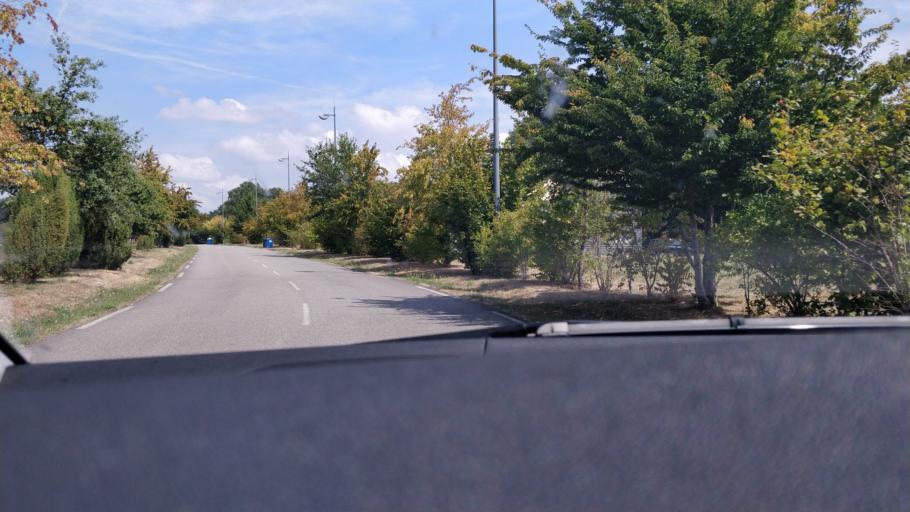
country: FR
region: Limousin
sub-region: Departement de la Haute-Vienne
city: Le Palais-sur-Vienne
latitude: 45.8556
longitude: 1.2977
